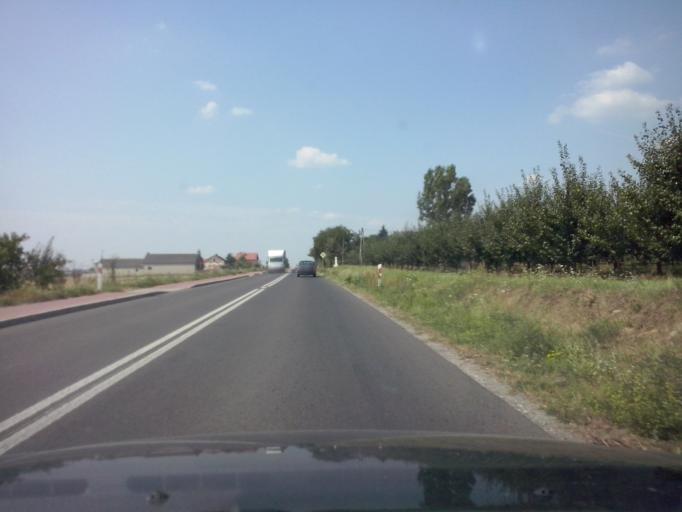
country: PL
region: Swietokrzyskie
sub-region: Powiat buski
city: Gnojno
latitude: 50.5863
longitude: 20.9177
